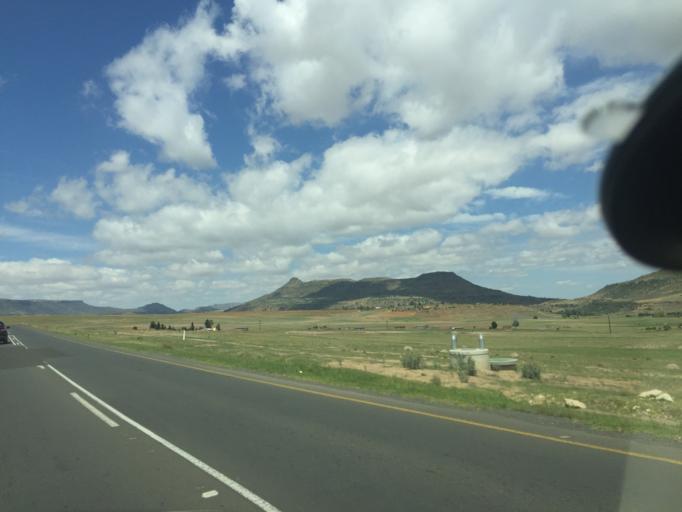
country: LS
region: Maseru
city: Maseru
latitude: -29.5299
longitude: 27.5153
